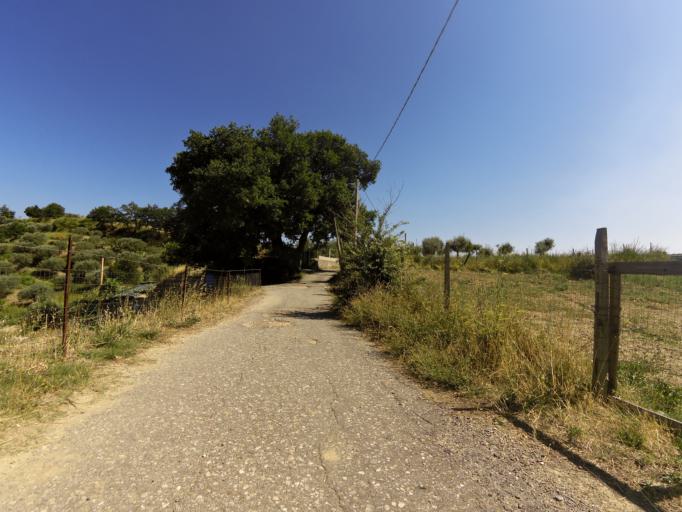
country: IT
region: Calabria
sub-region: Provincia di Reggio Calabria
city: Pazzano
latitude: 38.4612
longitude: 16.4545
